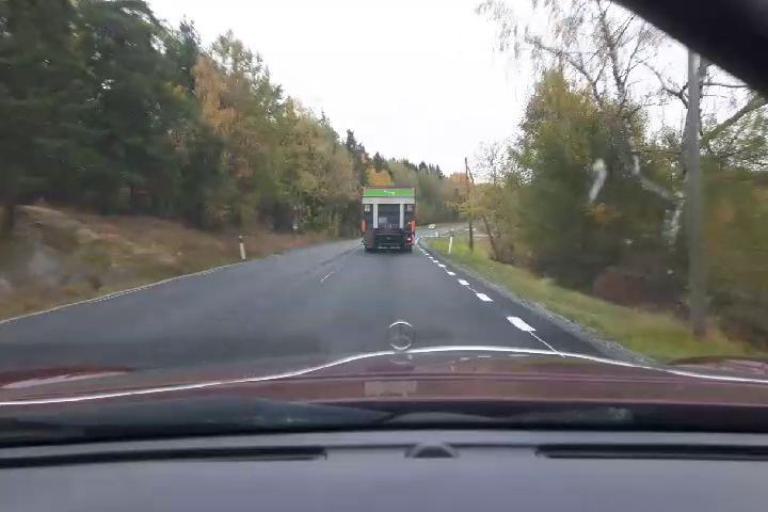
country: SE
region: Soedermanland
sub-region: Strangnas Kommun
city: Strangnas
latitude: 59.4356
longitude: 17.0230
